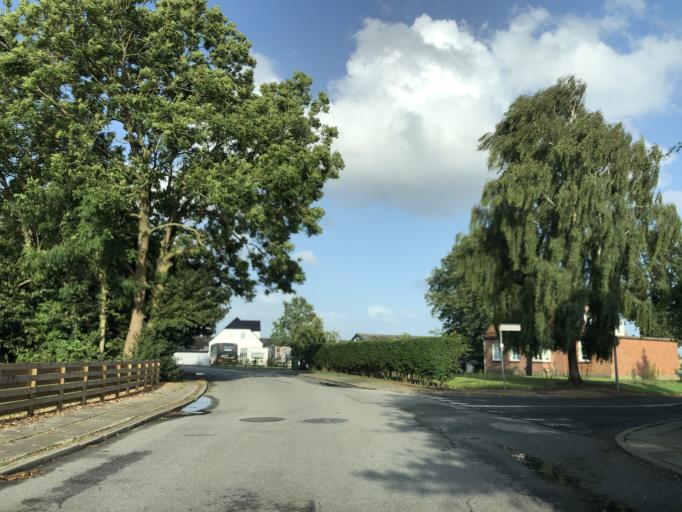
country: DK
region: South Denmark
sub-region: Haderslev Kommune
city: Starup
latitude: 55.1924
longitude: 9.5190
